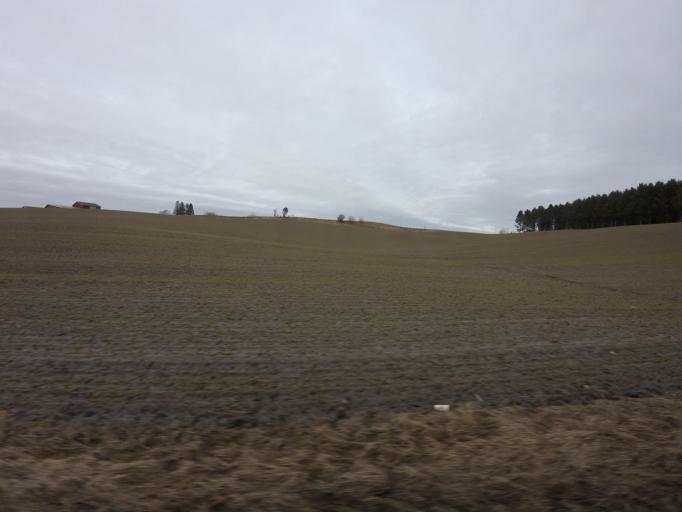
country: NO
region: Ostfold
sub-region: Trogstad
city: Skjonhaug
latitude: 59.6534
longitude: 11.3100
